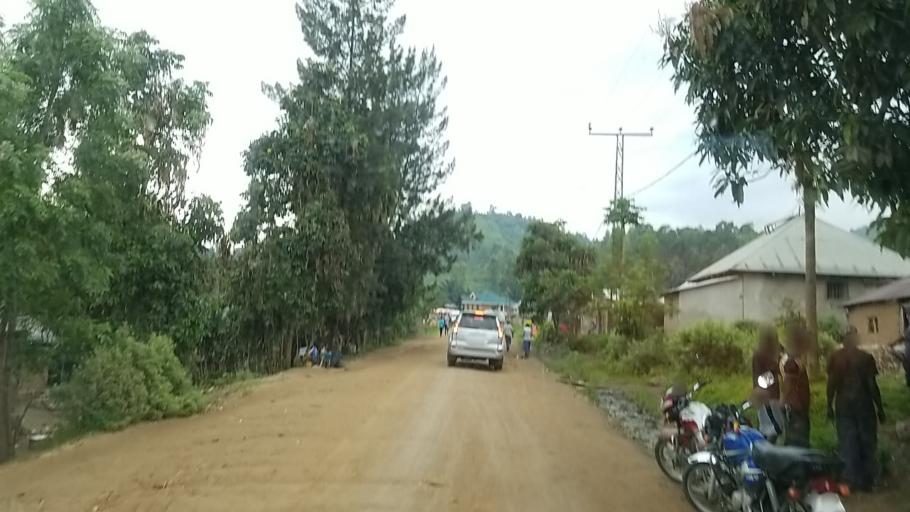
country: CD
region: Nord Kivu
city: Sake
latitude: -1.6977
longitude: 29.0137
